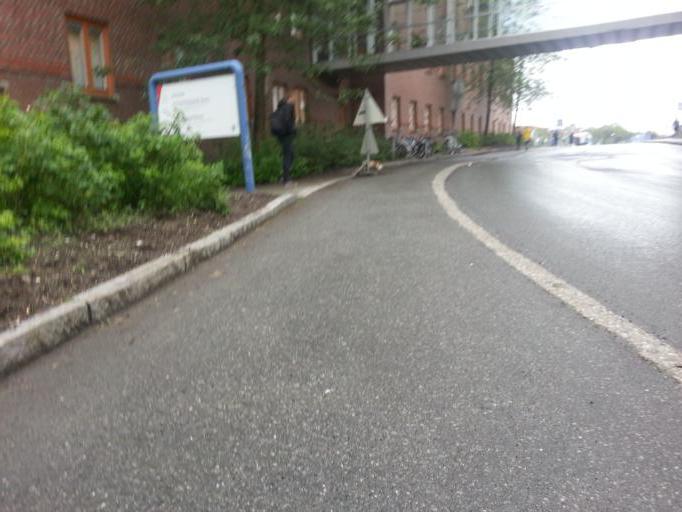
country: NO
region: Troms
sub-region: Tromso
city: Tromso
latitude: 69.6829
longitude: 18.9790
